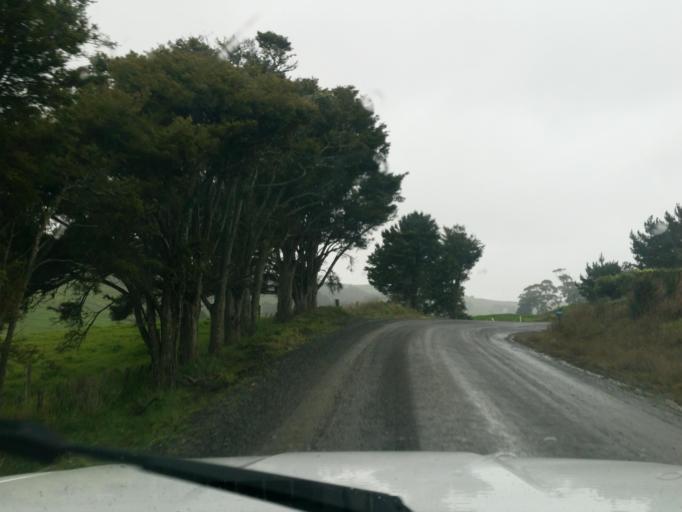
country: NZ
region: Northland
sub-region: Kaipara District
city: Dargaville
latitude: -35.9814
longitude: 174.0652
